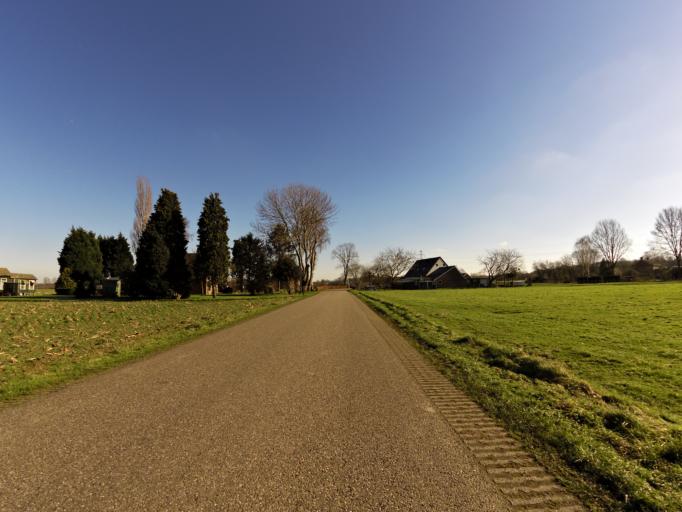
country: NL
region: Gelderland
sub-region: Gemeente Doesburg
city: Doesburg
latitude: 51.9387
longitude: 6.1594
